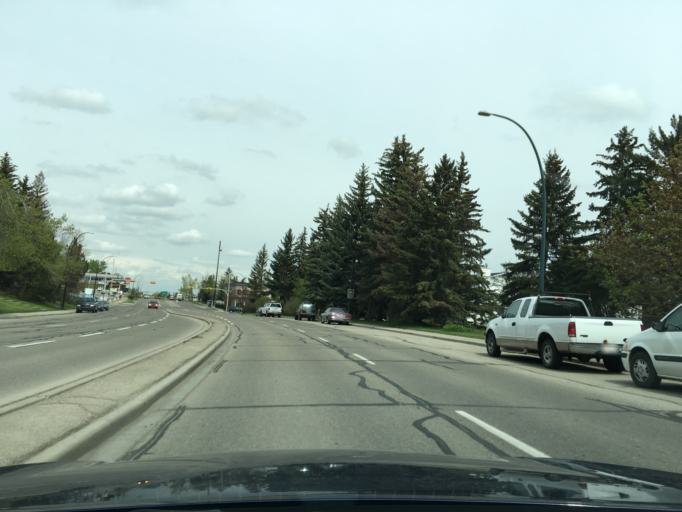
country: CA
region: Alberta
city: Calgary
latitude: 50.9464
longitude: -114.0846
